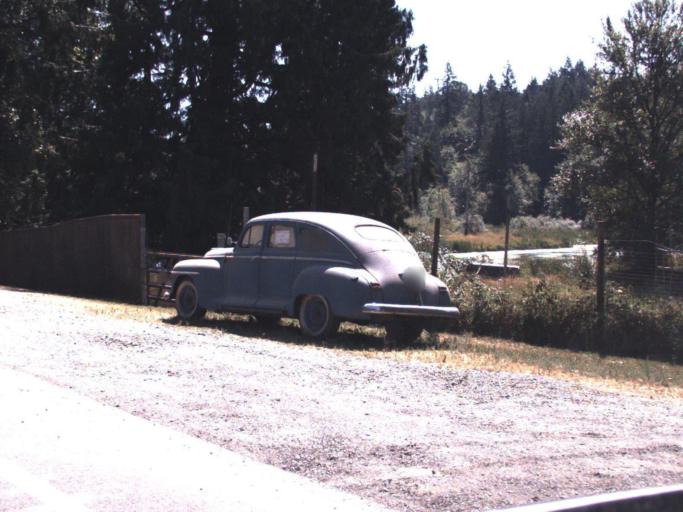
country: US
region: Washington
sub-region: King County
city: Ames Lake
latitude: 47.6274
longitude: -121.9833
